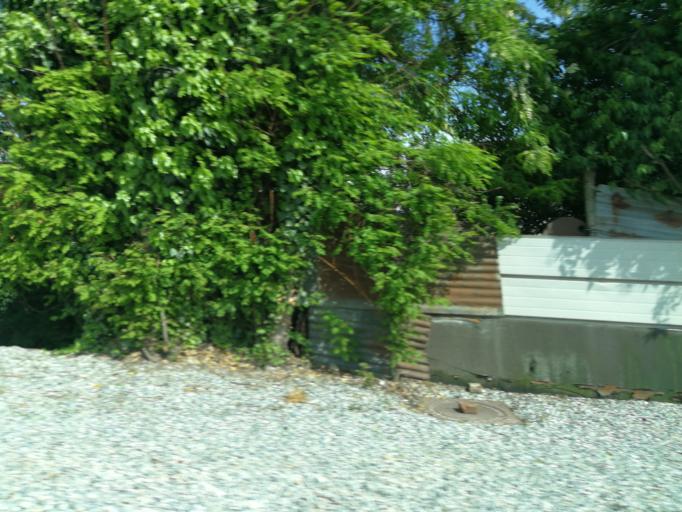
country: IT
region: Piedmont
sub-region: Provincia di Cuneo
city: Moretta
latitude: 44.7690
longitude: 7.5450
